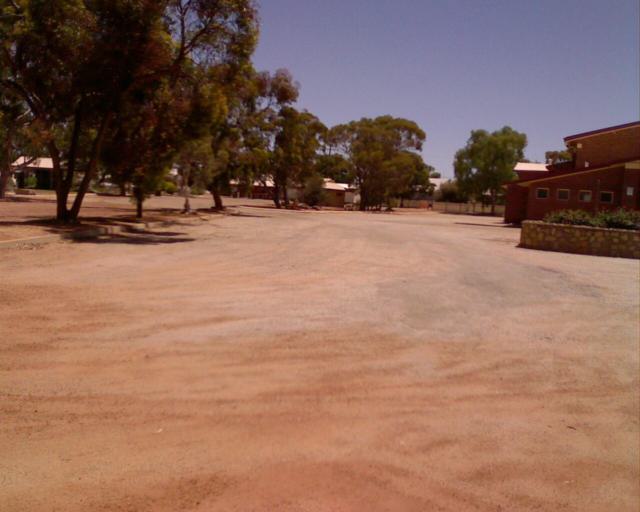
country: AU
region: Western Australia
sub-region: Wongan-Ballidu
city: Wongan Hills
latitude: -30.8277
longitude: 117.4817
